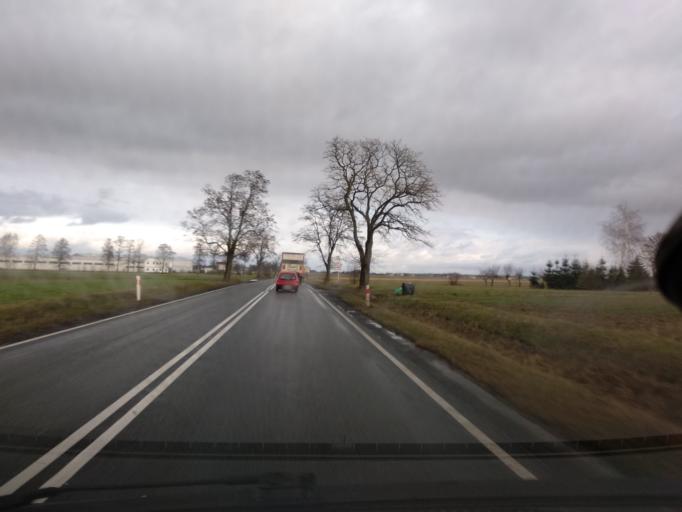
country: PL
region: Greater Poland Voivodeship
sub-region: Powiat koninski
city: Stare Miasto
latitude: 52.1442
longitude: 18.1956
